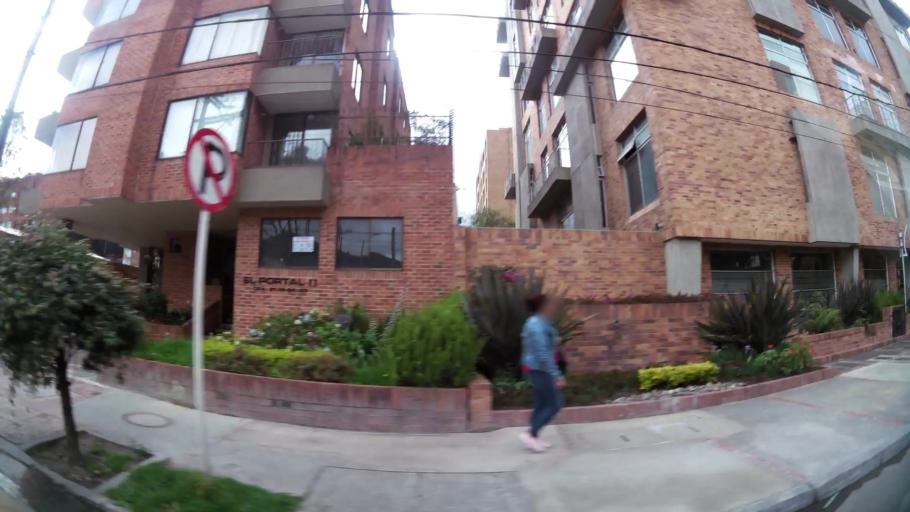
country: CO
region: Bogota D.C.
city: Barrio San Luis
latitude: 4.6818
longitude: -74.0553
